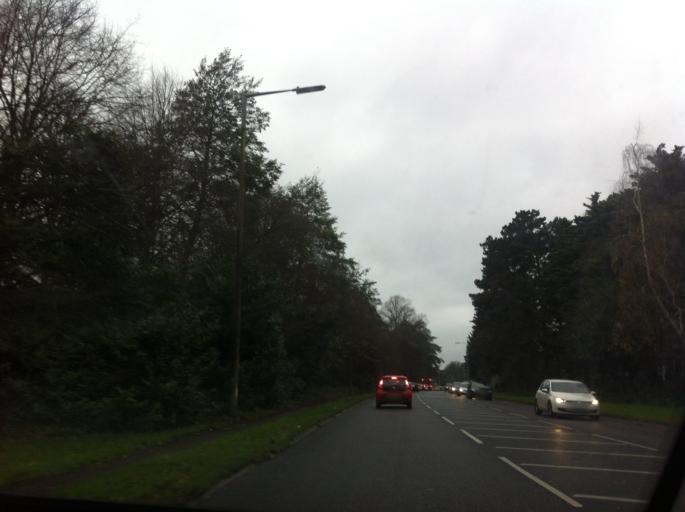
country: GB
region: England
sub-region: Northamptonshire
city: Earls Barton
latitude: 52.2652
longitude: -0.7342
